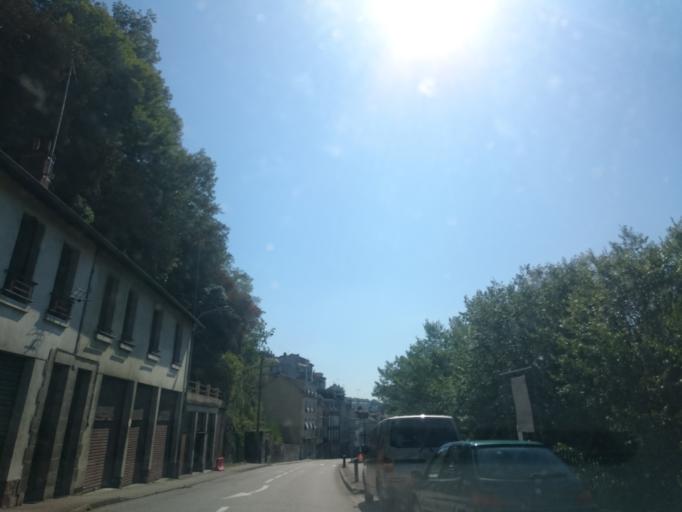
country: FR
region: Limousin
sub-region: Departement de la Correze
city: Tulle
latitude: 45.2709
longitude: 1.7766
